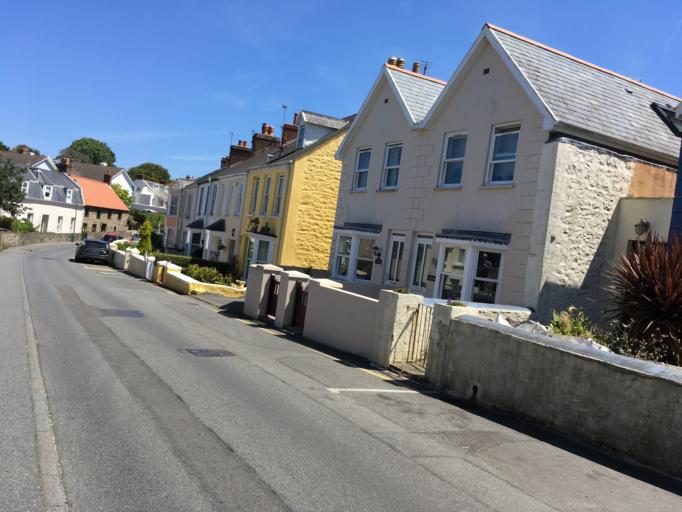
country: GG
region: St Peter Port
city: Saint Peter Port
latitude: 49.4594
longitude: -2.5485
